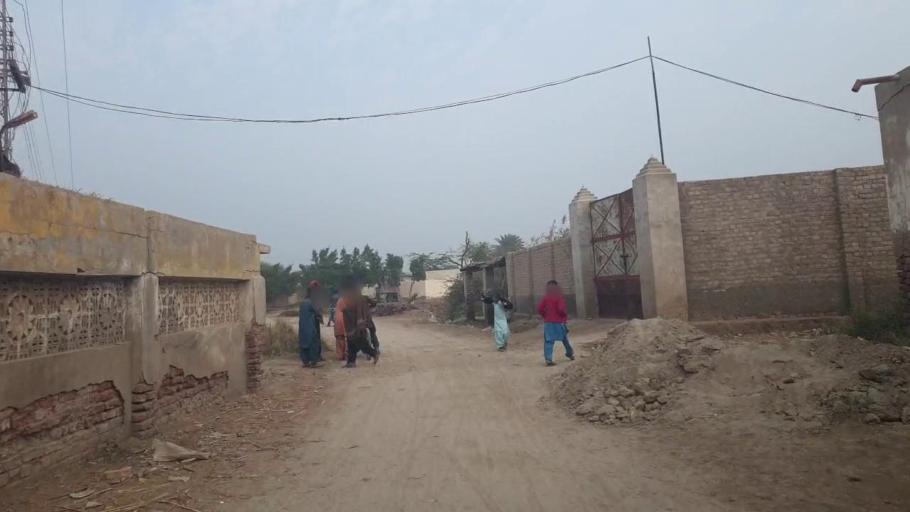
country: PK
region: Sindh
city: Berani
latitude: 25.8139
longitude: 68.7331
